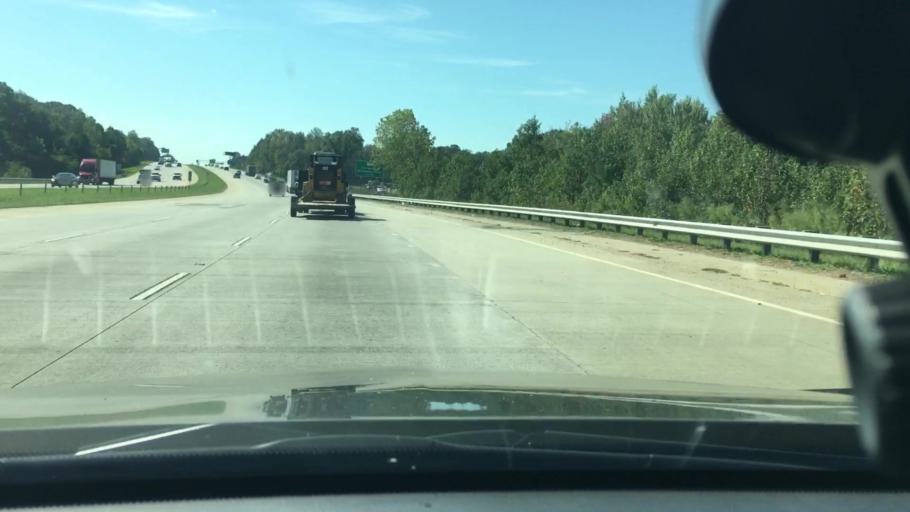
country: US
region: North Carolina
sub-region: Gaston County
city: Mount Holly
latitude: 35.2862
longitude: -80.9656
